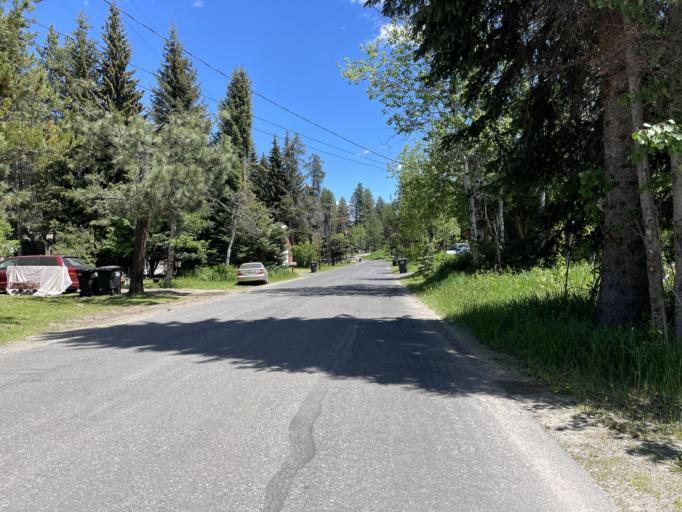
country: US
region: Idaho
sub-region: Valley County
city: McCall
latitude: 44.9060
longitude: -116.0956
